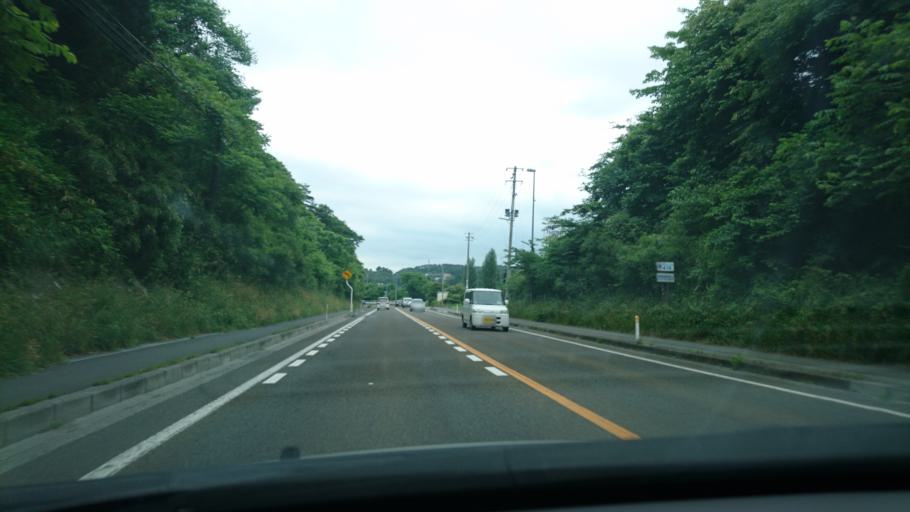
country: JP
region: Miyagi
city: Furukawa
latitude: 38.7267
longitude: 141.0214
